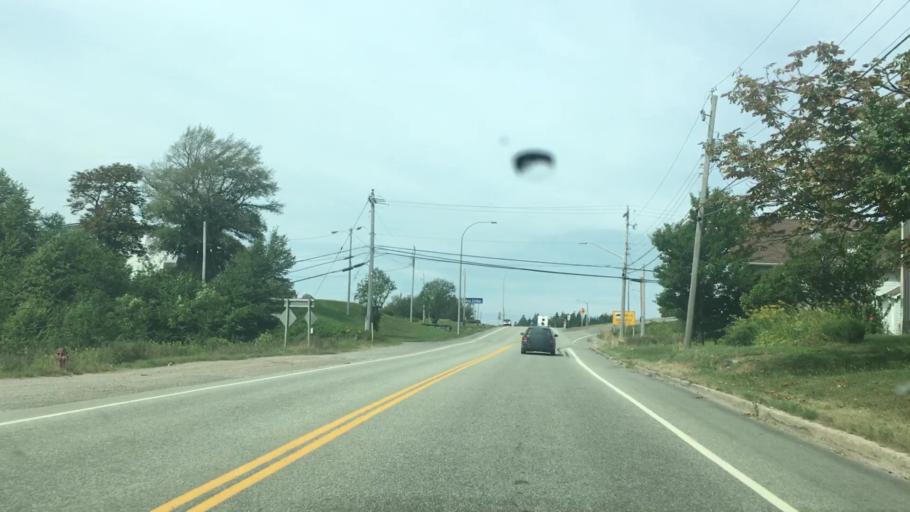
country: CA
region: Nova Scotia
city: Port Hawkesbury
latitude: 45.6450
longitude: -61.4002
